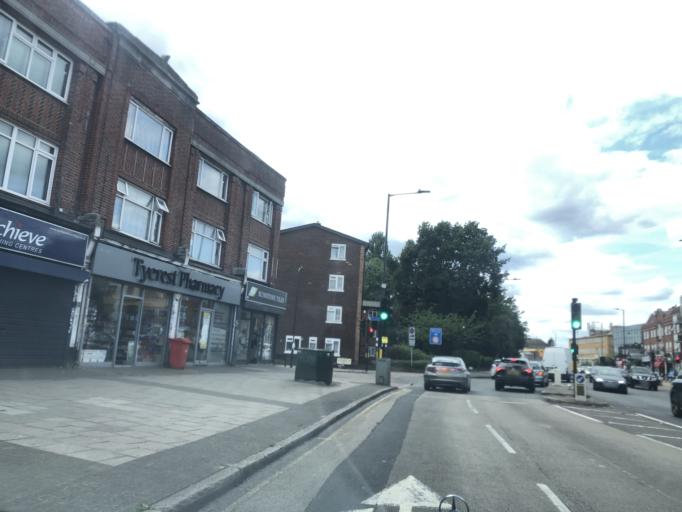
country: GB
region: England
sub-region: Greater London
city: Wembley
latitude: 51.5868
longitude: -0.2987
